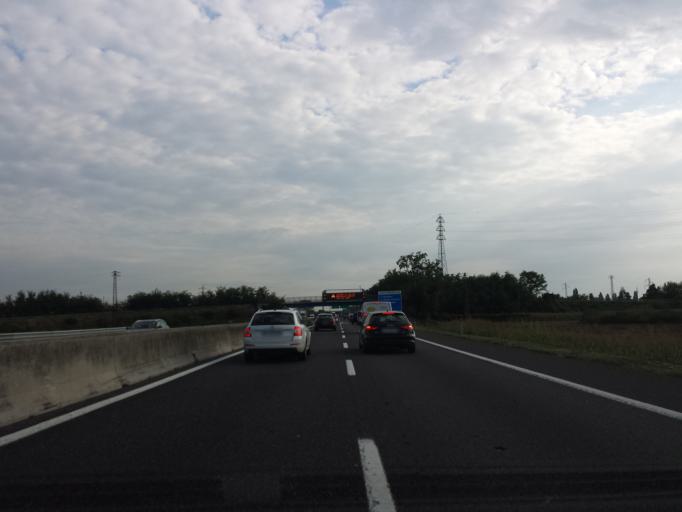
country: IT
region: Veneto
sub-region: Provincia di Padova
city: Pernumia
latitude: 45.2462
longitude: 11.7745
